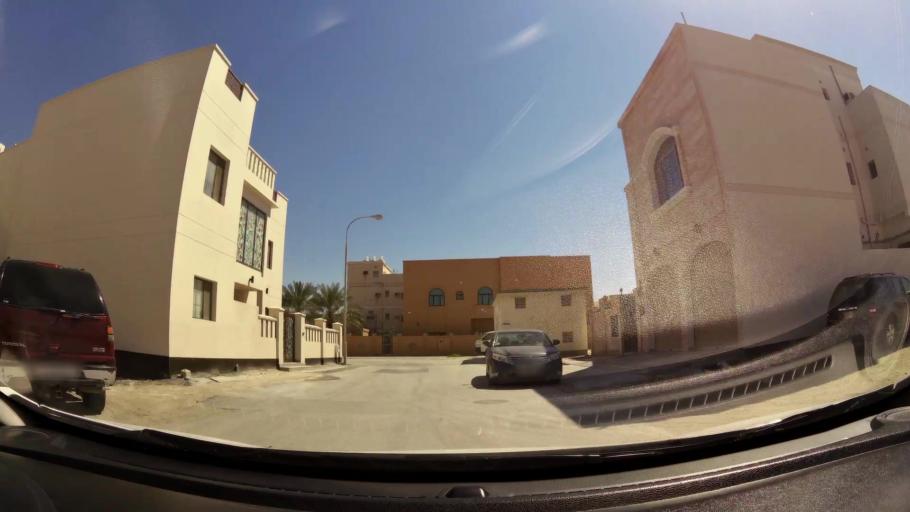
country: BH
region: Muharraq
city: Al Muharraq
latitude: 26.2782
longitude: 50.6370
